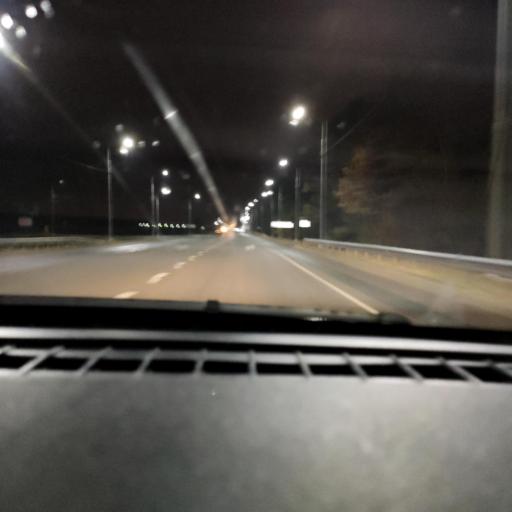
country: RU
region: Voronezj
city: Somovo
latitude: 51.6976
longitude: 39.3980
